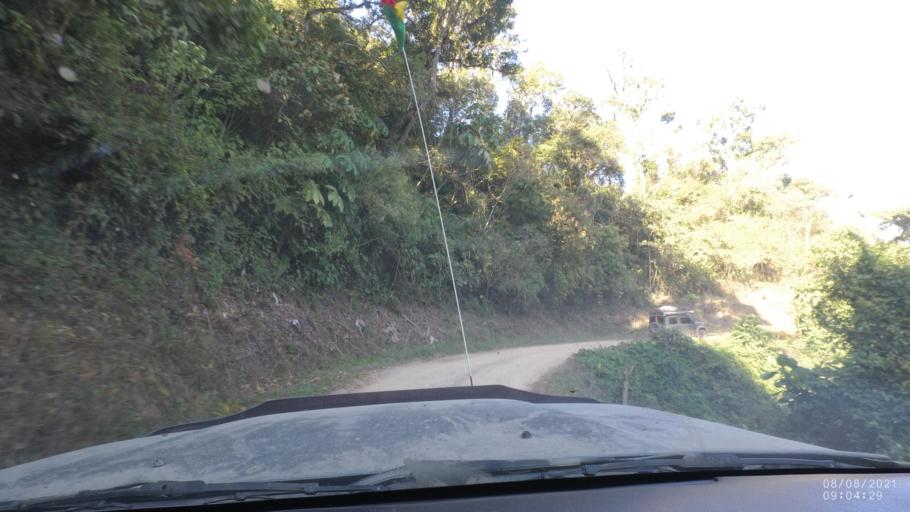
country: BO
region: La Paz
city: Quime
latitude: -16.5554
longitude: -66.7364
